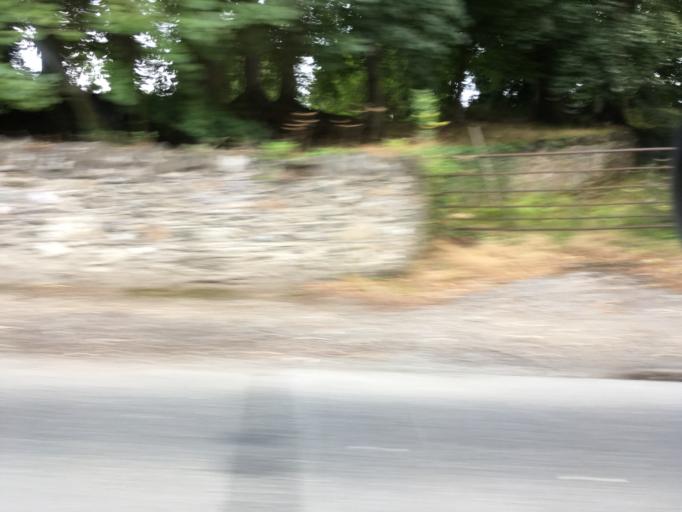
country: IE
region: Leinster
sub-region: Wicklow
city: Ashford
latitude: 53.0158
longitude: -6.1053
